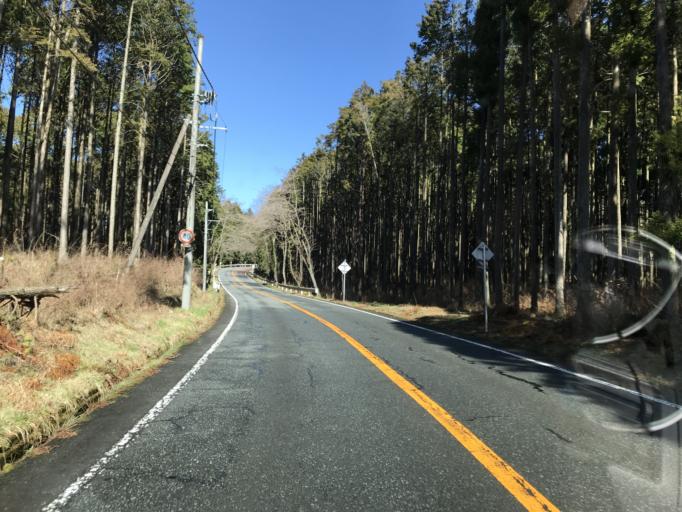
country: JP
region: Shizuoka
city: Fujinomiya
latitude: 35.2889
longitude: 138.6626
